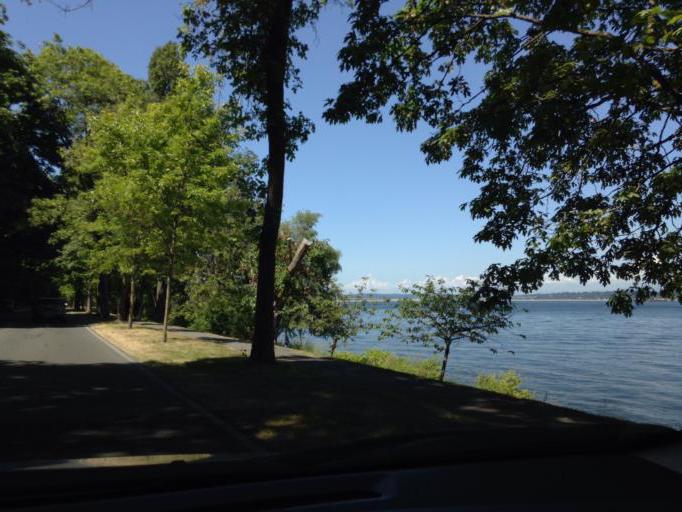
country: US
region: Washington
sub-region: King County
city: Seattle
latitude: 47.5766
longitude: -122.2828
